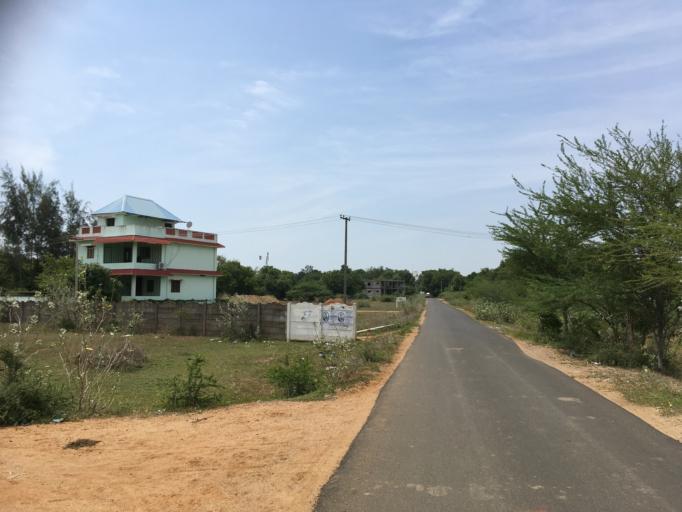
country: IN
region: Tamil Nadu
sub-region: Villupuram
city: Auroville
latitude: 12.0087
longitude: 79.7960
